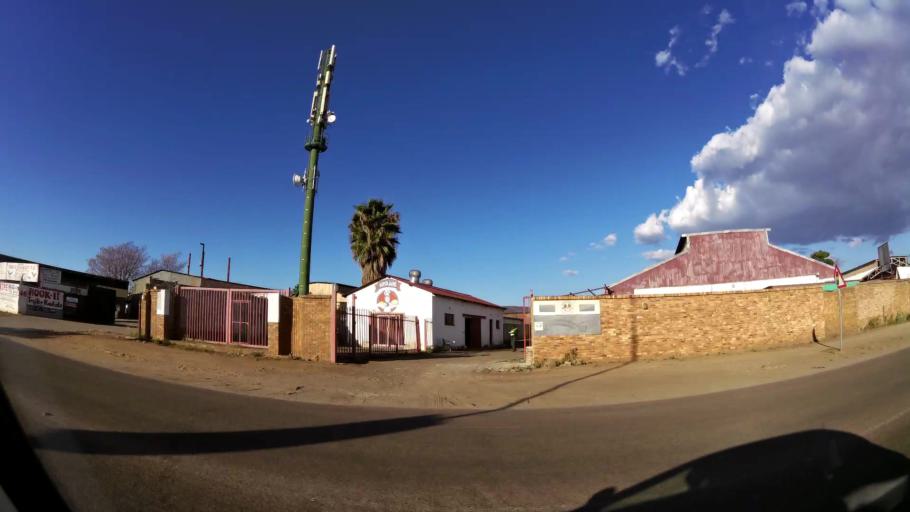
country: ZA
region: Limpopo
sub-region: Waterberg District Municipality
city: Mokopane
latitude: -24.1760
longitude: 29.0020
